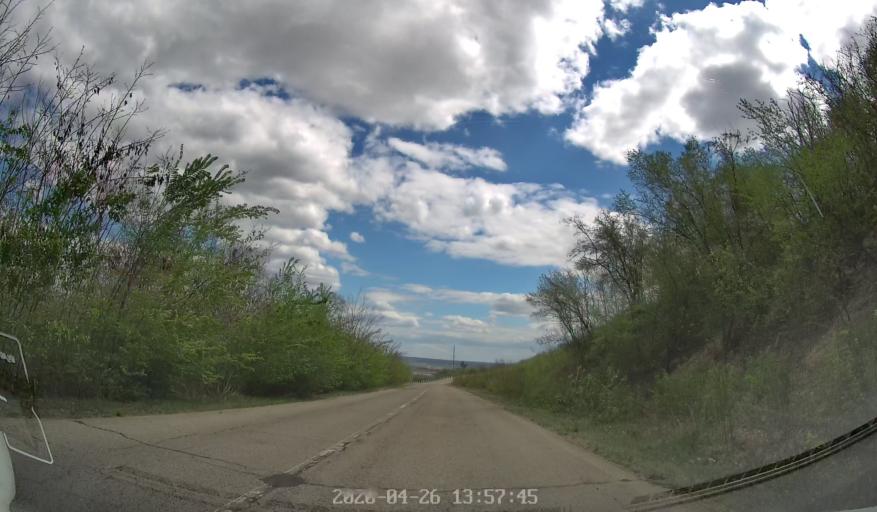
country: MD
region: Telenesti
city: Cocieri
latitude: 47.2724
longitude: 29.1185
